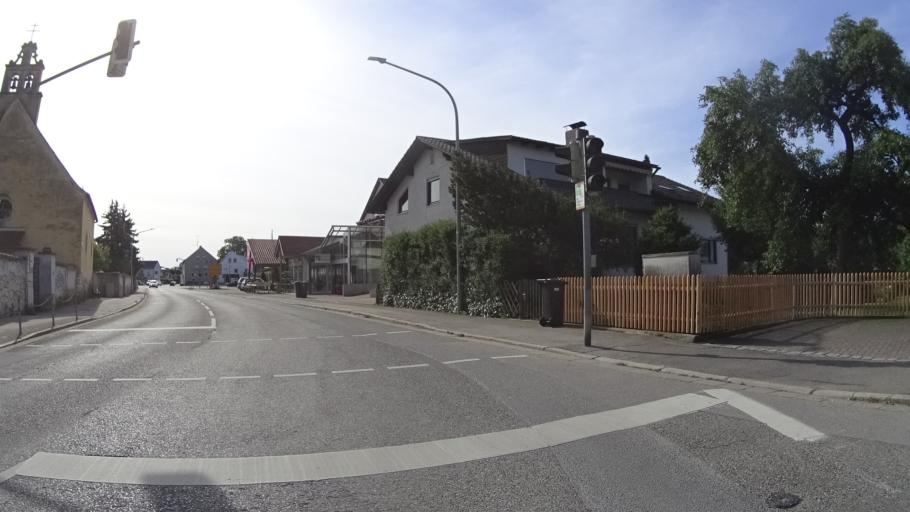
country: DE
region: Bavaria
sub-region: Lower Bavaria
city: Kelheim
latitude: 48.9196
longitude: 11.8795
